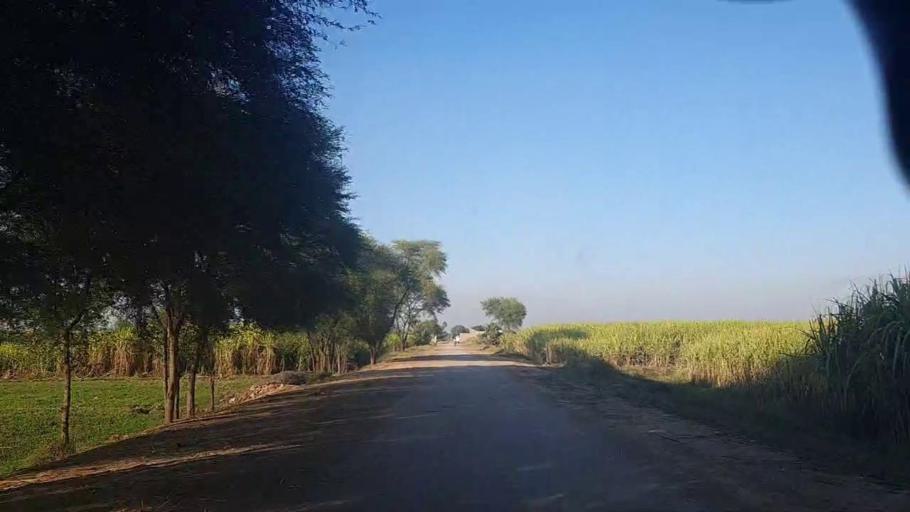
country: PK
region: Sindh
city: Sobhadero
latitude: 27.4145
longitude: 68.4228
